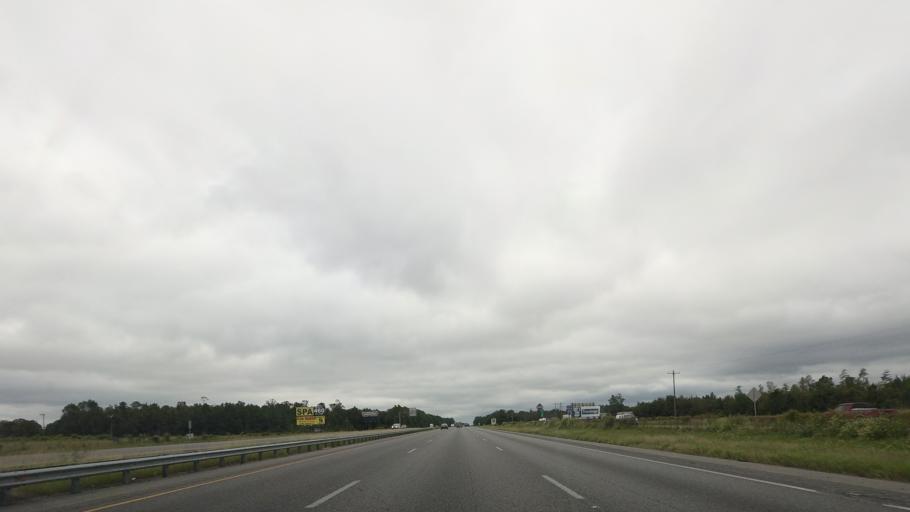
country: US
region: Georgia
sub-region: Lowndes County
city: Valdosta
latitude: 30.7446
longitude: -83.2699
